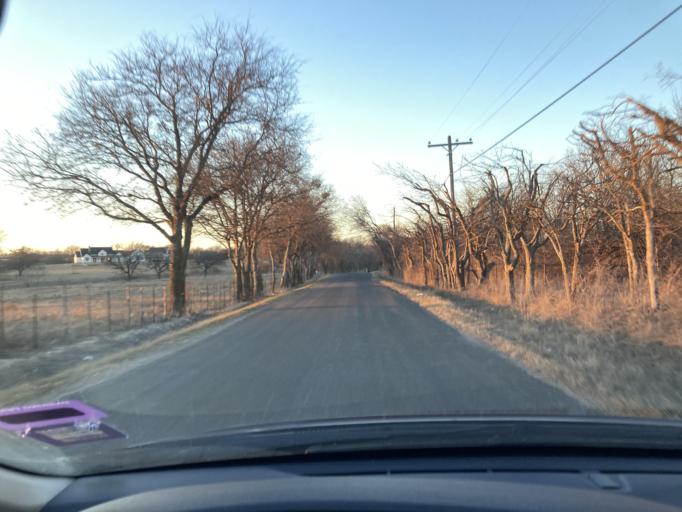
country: US
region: Texas
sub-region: Ellis County
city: Nash
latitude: 32.2891
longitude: -96.9090
